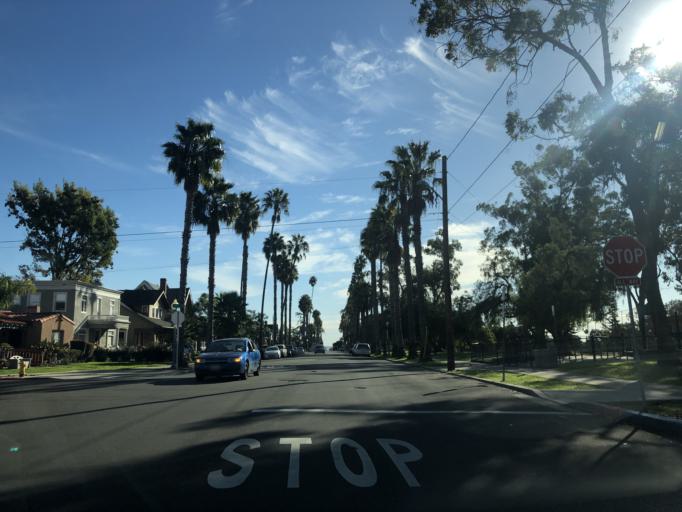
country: US
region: California
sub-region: San Diego County
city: San Diego
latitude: 32.7226
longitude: -117.1339
